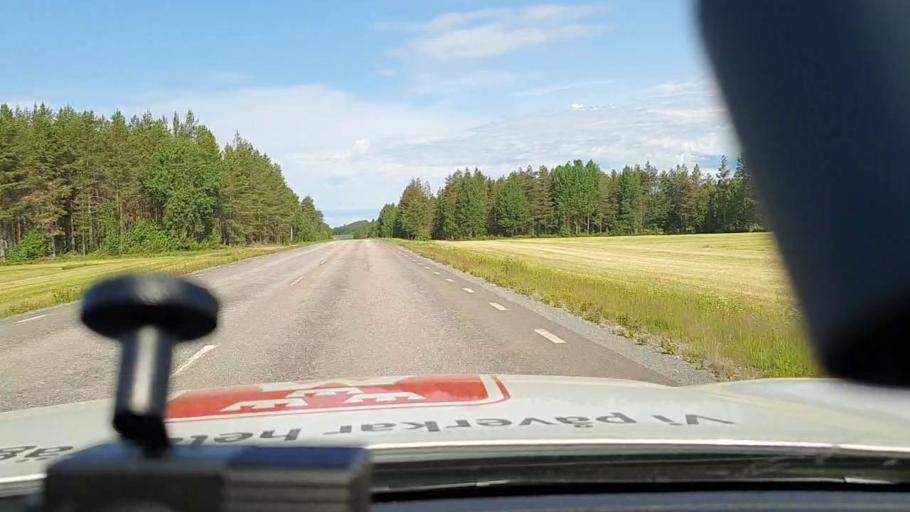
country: SE
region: Norrbotten
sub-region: Bodens Kommun
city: Boden
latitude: 65.9059
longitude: 21.3618
